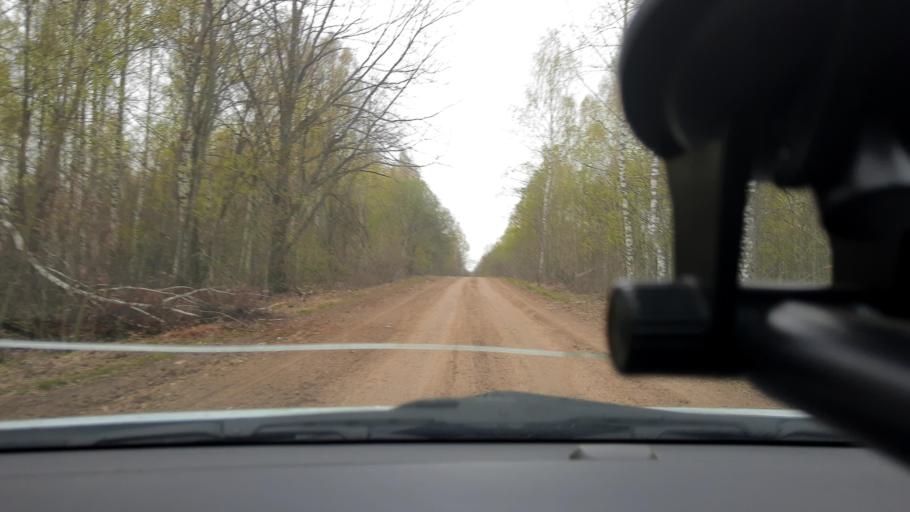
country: RU
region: Bashkortostan
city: Pavlovka
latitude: 55.4344
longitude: 56.3570
